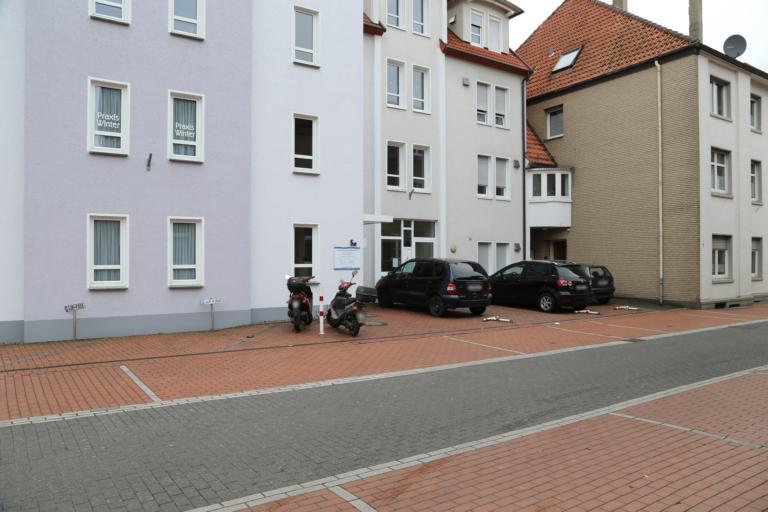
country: DE
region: North Rhine-Westphalia
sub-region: Regierungsbezirk Detmold
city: Lage
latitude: 51.9918
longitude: 8.7917
